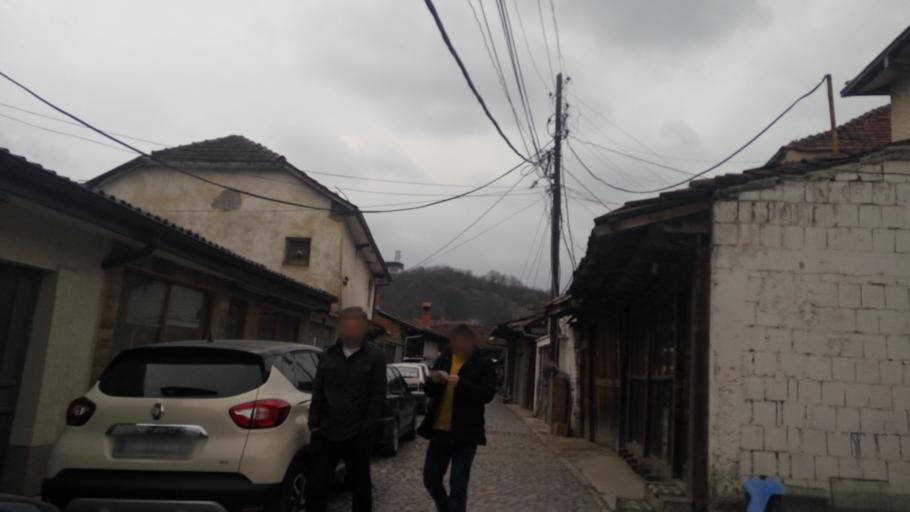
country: XK
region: Gjakova
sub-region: Komuna e Gjakoves
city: Gjakove
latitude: 42.3808
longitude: 20.4277
